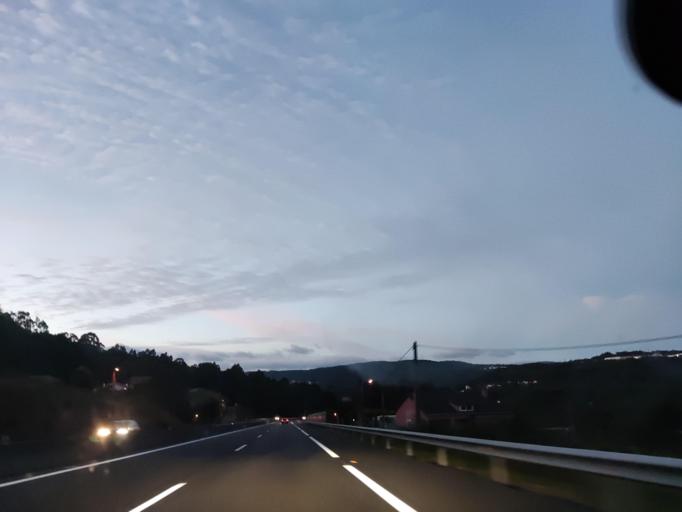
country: ES
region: Galicia
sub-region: Provincia da Coruna
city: Boiro
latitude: 42.6511
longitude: -8.9024
